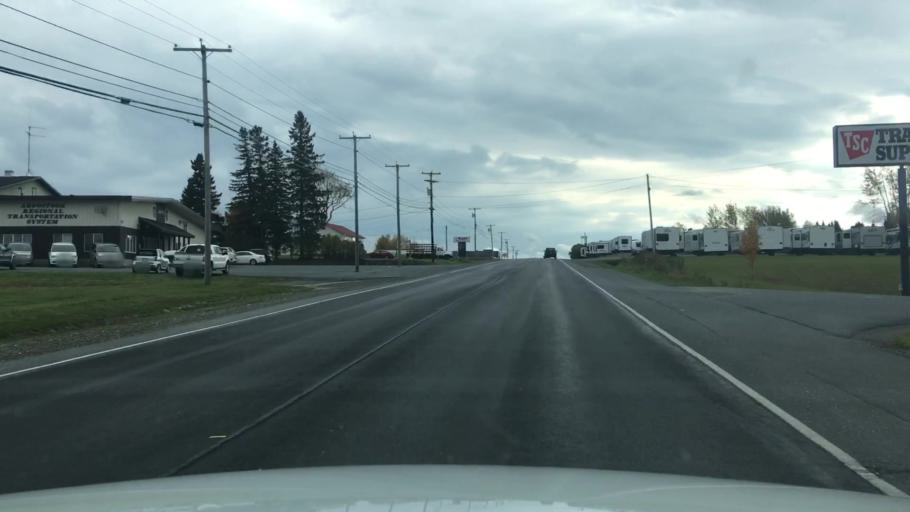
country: US
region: Maine
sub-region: Aroostook County
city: Presque Isle
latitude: 46.6613
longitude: -68.0084
